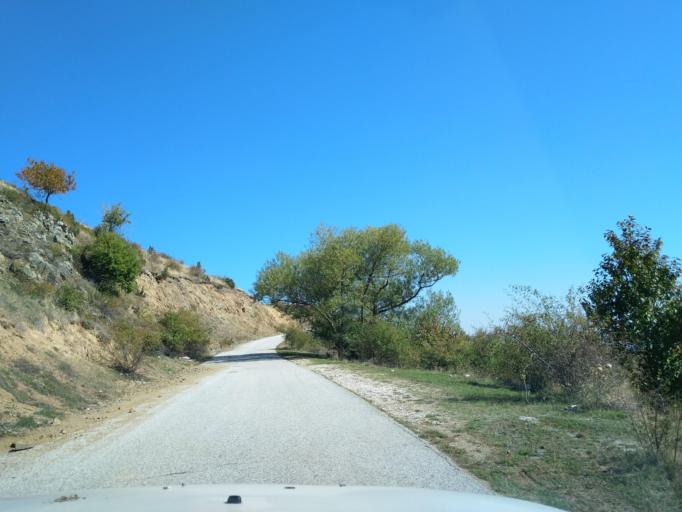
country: RS
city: Sokolovica
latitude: 43.2542
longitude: 20.3395
